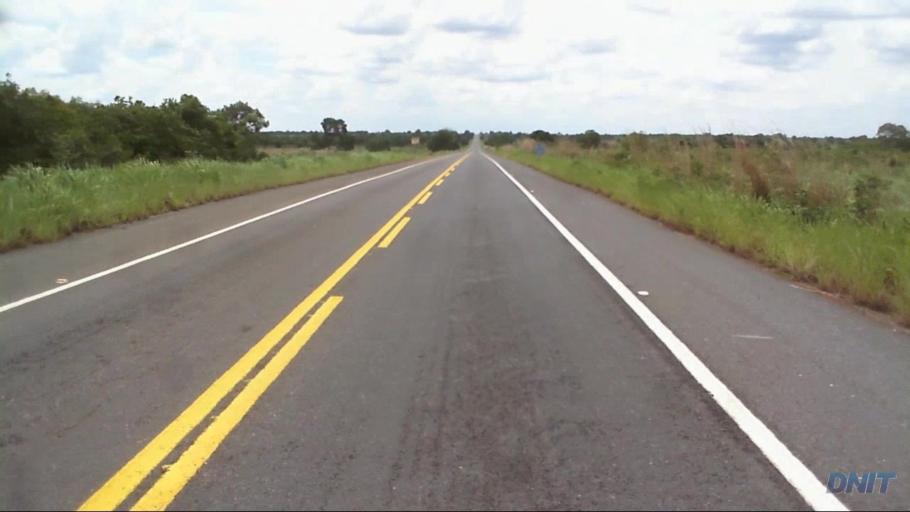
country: BR
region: Goias
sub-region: Sao Miguel Do Araguaia
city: Sao Miguel do Araguaia
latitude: -13.2922
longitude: -50.4026
